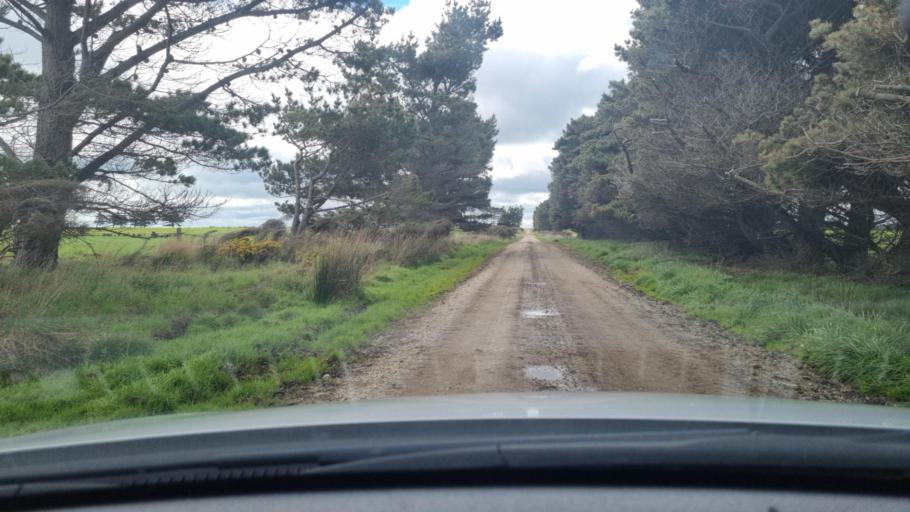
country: NZ
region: Southland
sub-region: Invercargill City
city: Bluff
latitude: -46.5707
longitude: 168.4991
